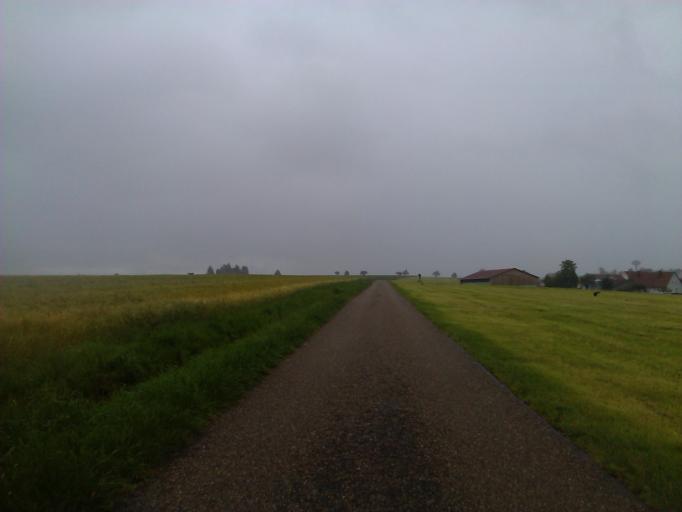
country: DE
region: Baden-Wuerttemberg
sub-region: Regierungsbezirk Stuttgart
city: Abtsgmund
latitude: 48.8771
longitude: 10.0192
